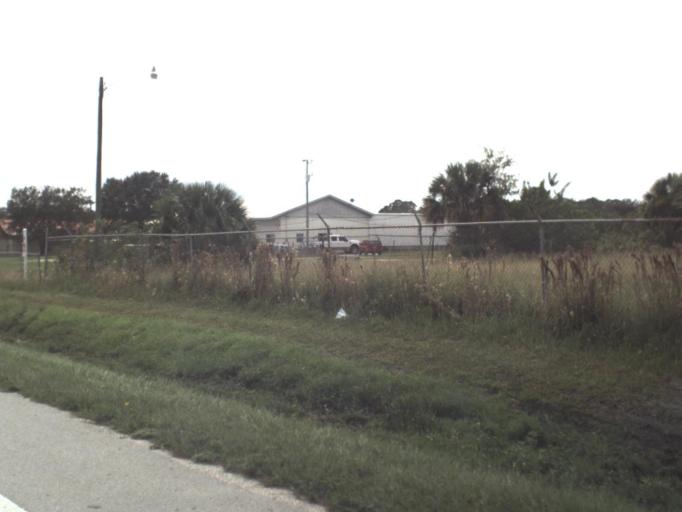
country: US
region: Florida
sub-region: Lee County
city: Fort Myers Shores
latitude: 26.7392
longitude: -81.7611
